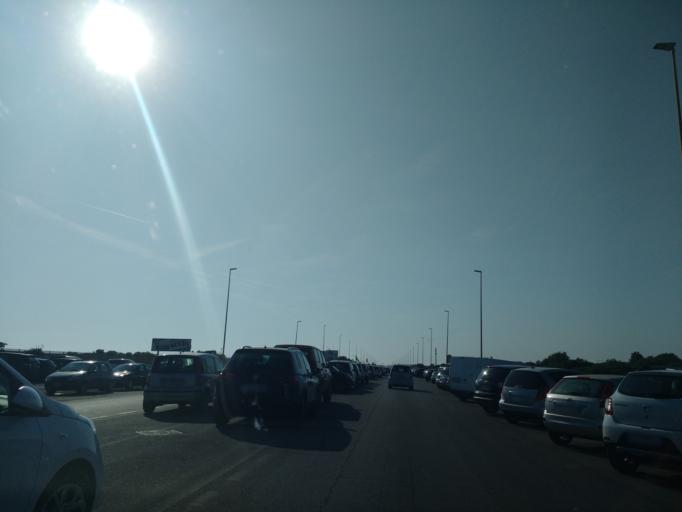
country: IT
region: Latium
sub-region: Citta metropolitana di Roma Capitale
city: Acilia-Castel Fusano-Ostia Antica
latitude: 41.7041
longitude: 12.3410
